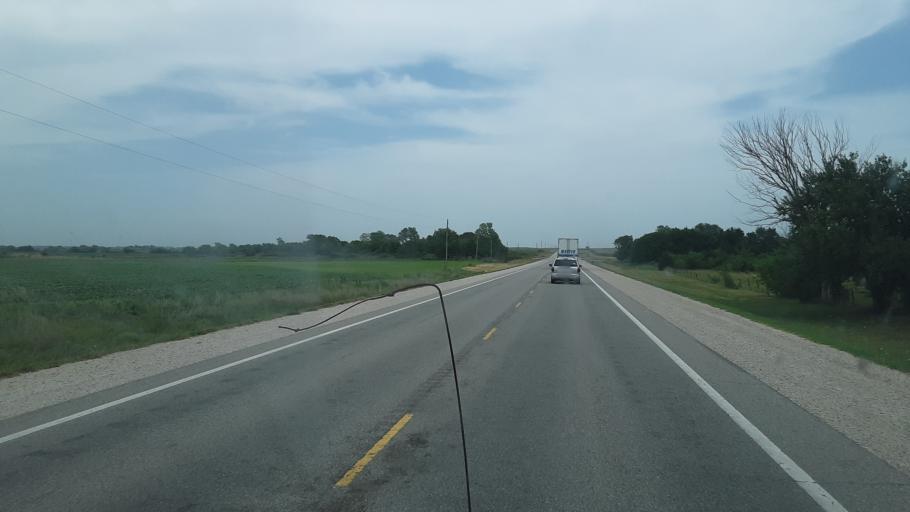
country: US
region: Kansas
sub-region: Allen County
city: Iola
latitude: 37.9215
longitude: -95.2610
